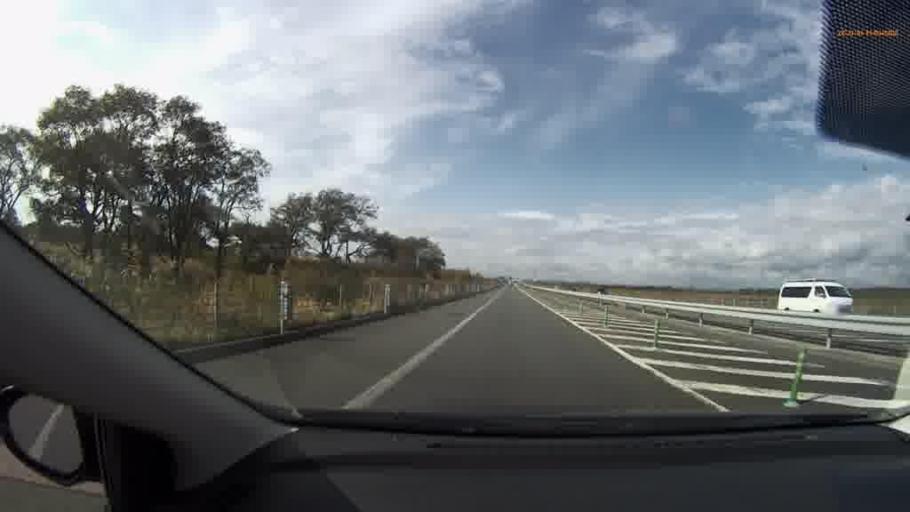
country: JP
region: Hokkaido
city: Kushiro
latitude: 43.0371
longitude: 144.3428
